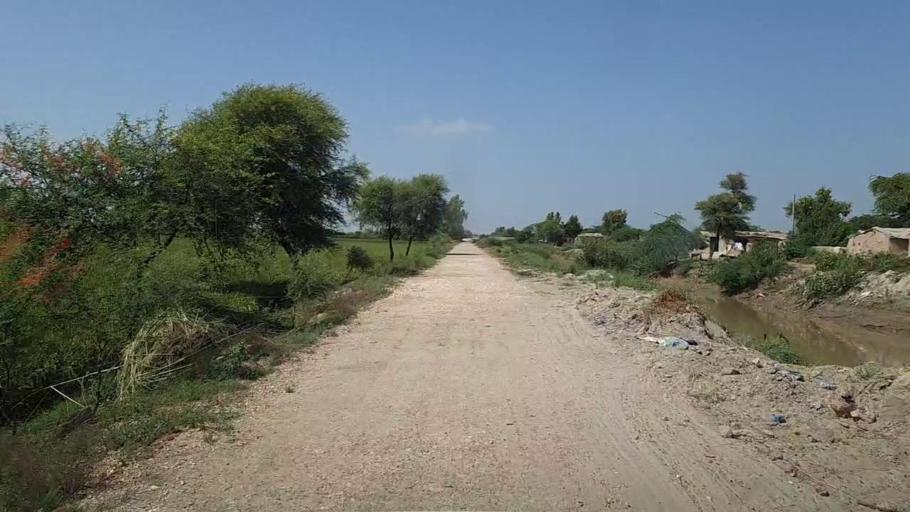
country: PK
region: Sindh
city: Kario
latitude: 24.6592
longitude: 68.5493
